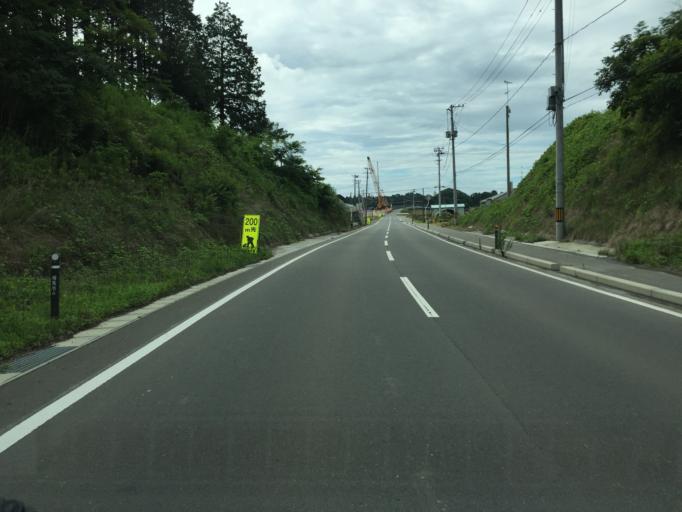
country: JP
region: Miyagi
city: Marumori
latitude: 37.8122
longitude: 140.9544
